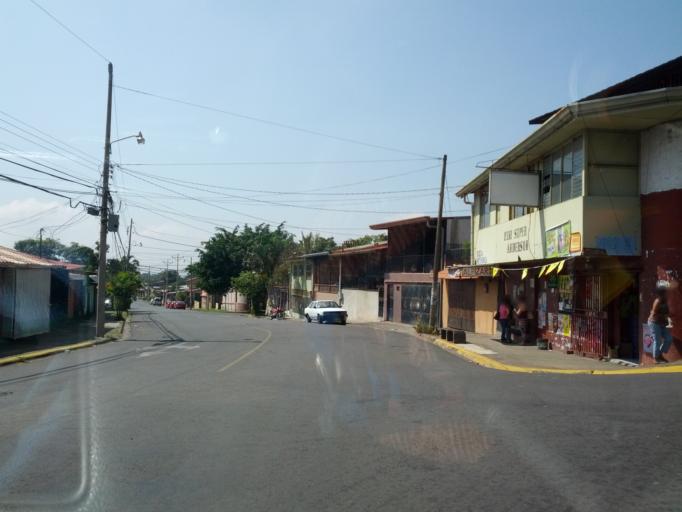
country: CR
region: Alajuela
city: Alajuela
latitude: 10.0157
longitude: -84.2020
